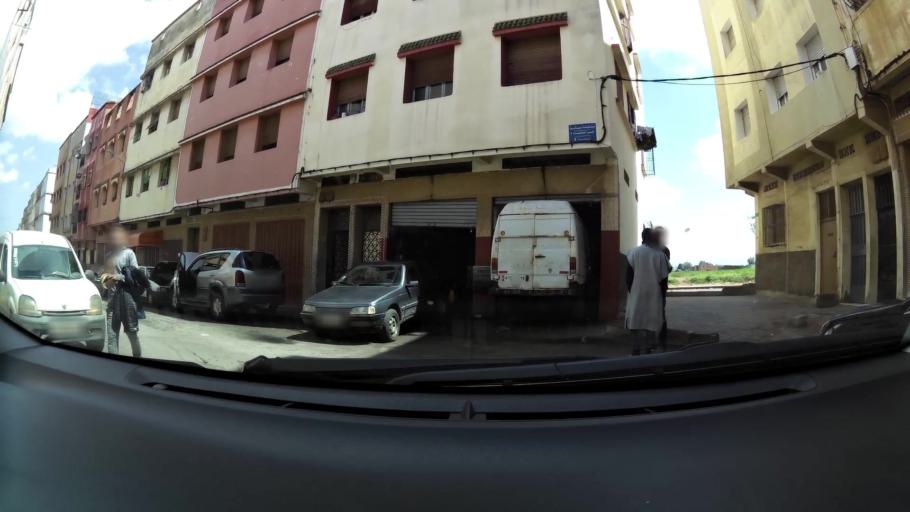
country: MA
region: Grand Casablanca
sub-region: Casablanca
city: Casablanca
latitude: 33.5365
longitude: -7.5666
